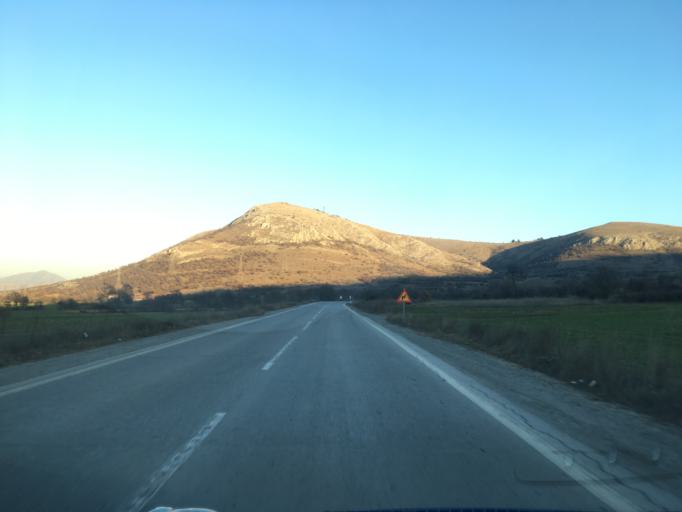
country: GR
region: West Macedonia
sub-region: Nomos Kozanis
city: Kozani
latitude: 40.3166
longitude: 21.7542
